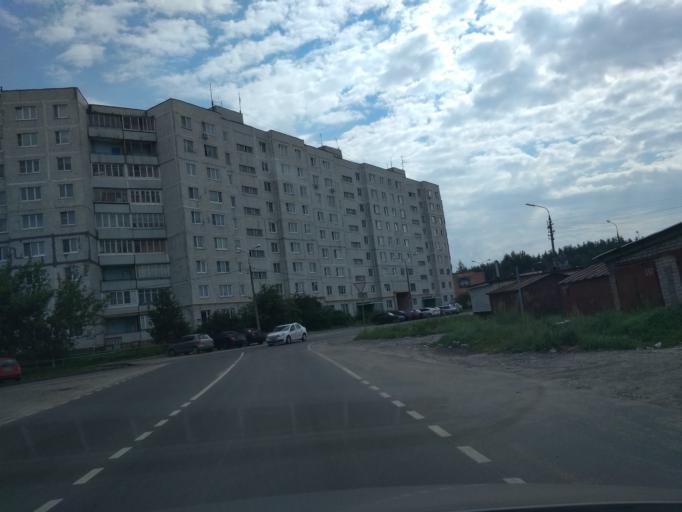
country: RU
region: Moskovskaya
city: Orekhovo-Zuyevo
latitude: 55.7939
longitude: 38.9371
